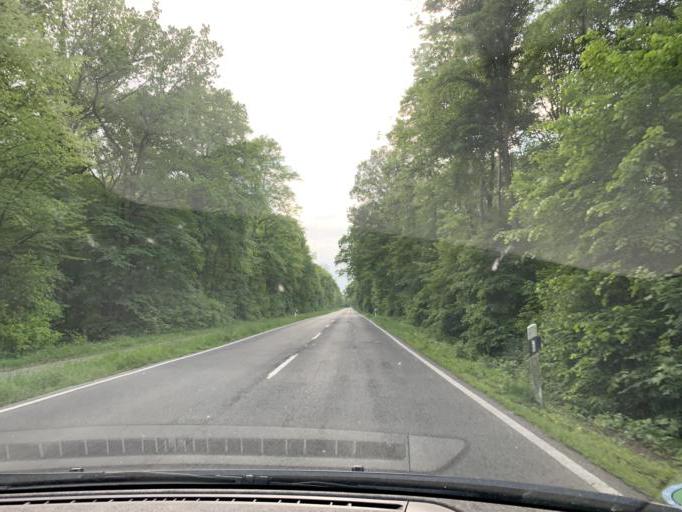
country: DE
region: North Rhine-Westphalia
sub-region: Regierungsbezirk Koln
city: Weilerswist
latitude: 50.7780
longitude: 6.8528
